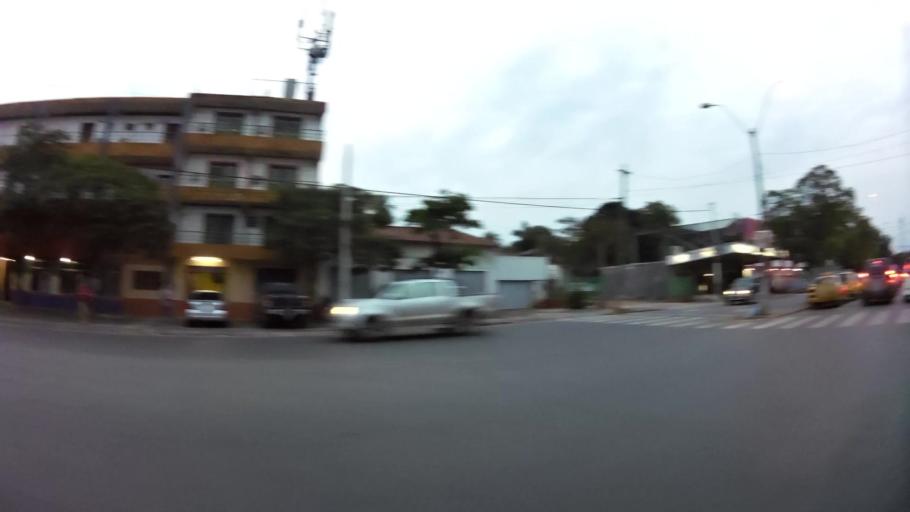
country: PY
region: Central
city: Lambare
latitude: -25.3269
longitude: -57.5978
